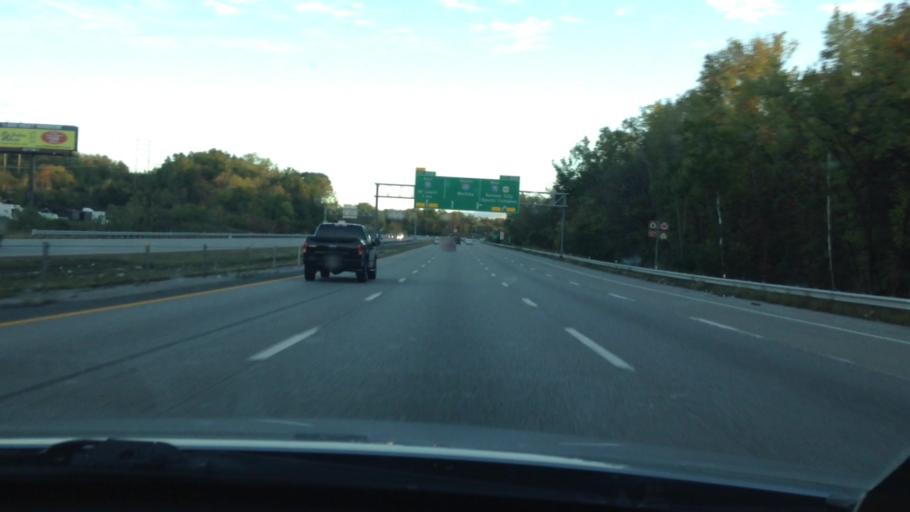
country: US
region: Missouri
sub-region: Jackson County
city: Sugar Creek
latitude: 39.0771
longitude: -94.4903
